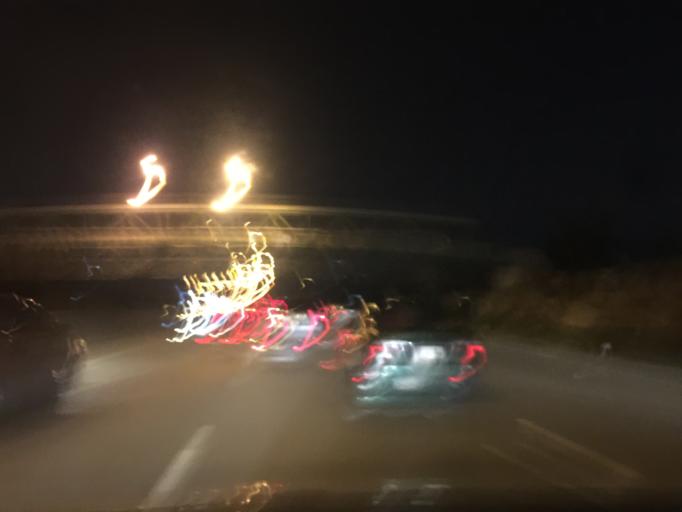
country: JO
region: Amman
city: Umm as Summaq
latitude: 31.9232
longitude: 35.8598
